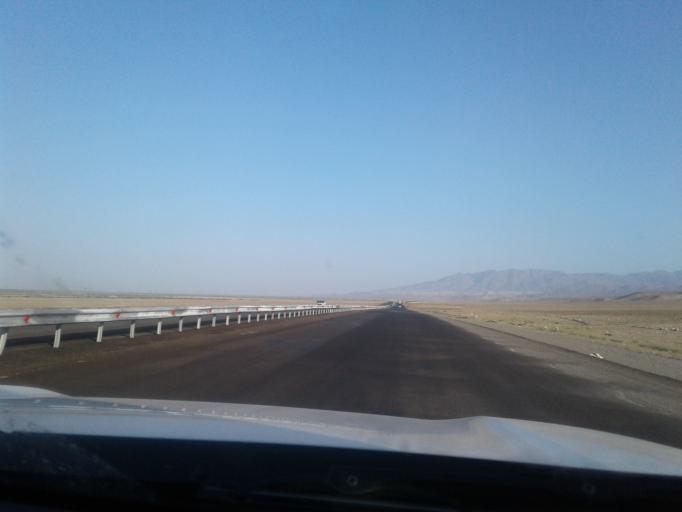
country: TM
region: Balkan
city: Magtymguly
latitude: 38.7046
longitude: 56.8142
